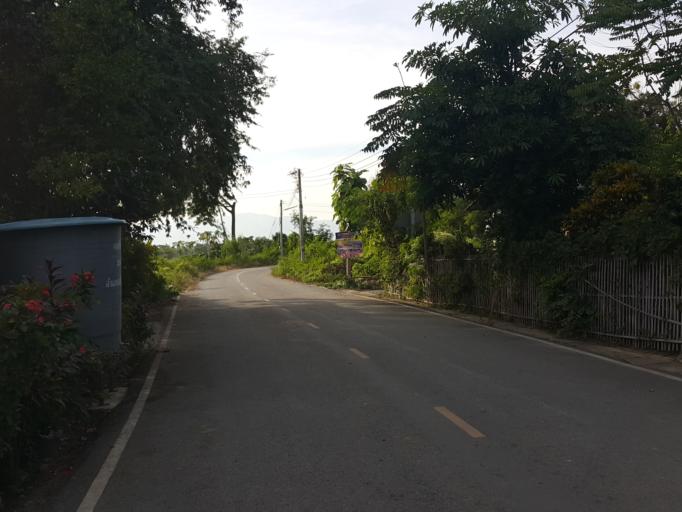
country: TH
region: Chiang Mai
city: San Kamphaeng
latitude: 18.7951
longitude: 99.1239
